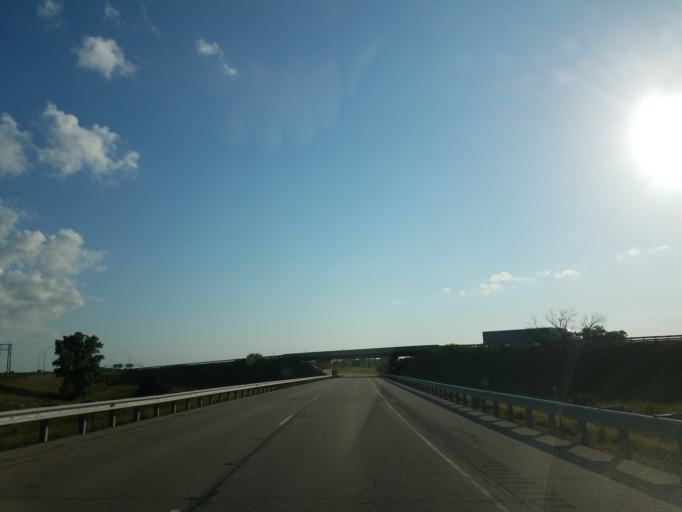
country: US
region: Illinois
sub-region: McLean County
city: Bloomington
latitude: 40.4395
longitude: -89.0220
